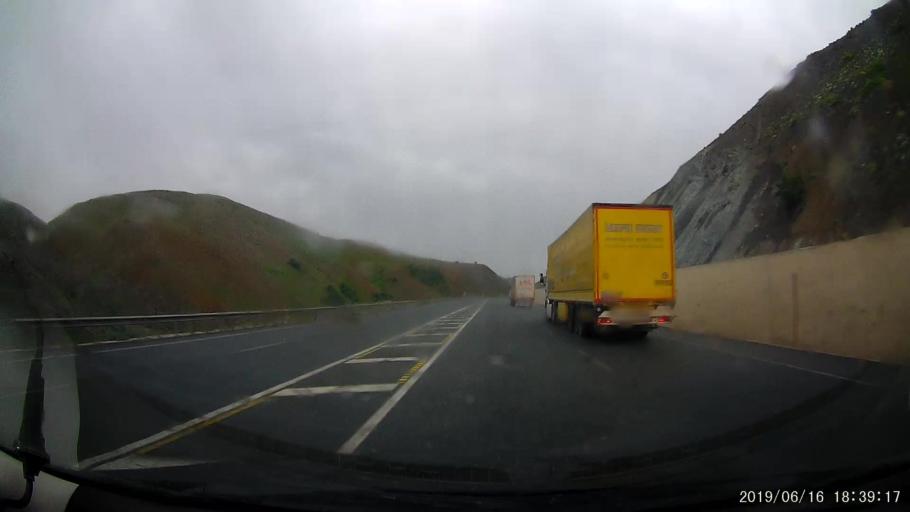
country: TR
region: Erzincan
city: Catalarmut
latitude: 39.8822
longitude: 39.1682
